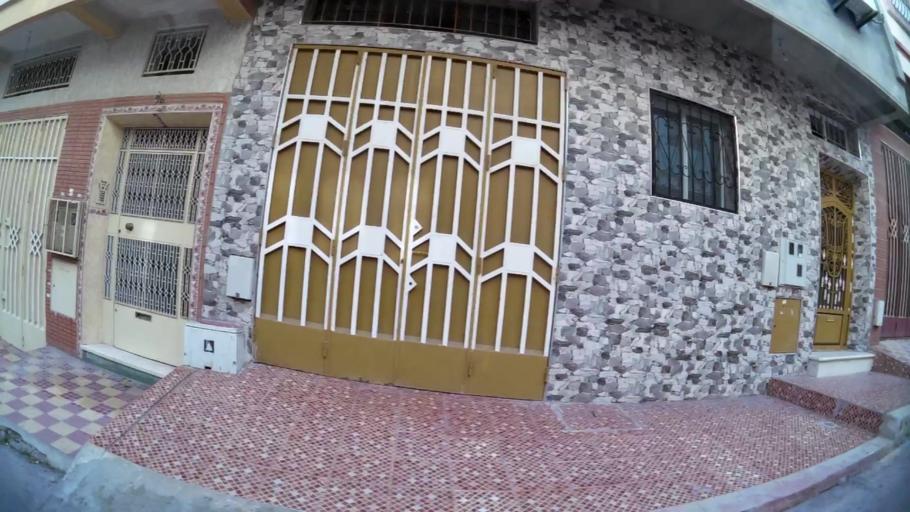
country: MA
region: Tanger-Tetouan
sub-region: Tanger-Assilah
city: Tangier
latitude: 35.7639
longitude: -5.8336
